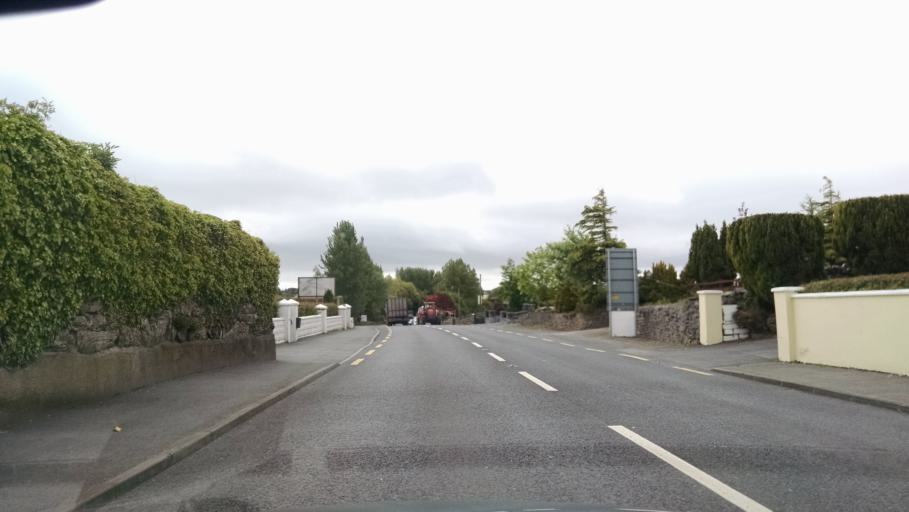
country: IE
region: Connaught
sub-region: County Galway
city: Moycullen
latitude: 53.4677
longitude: -9.1061
